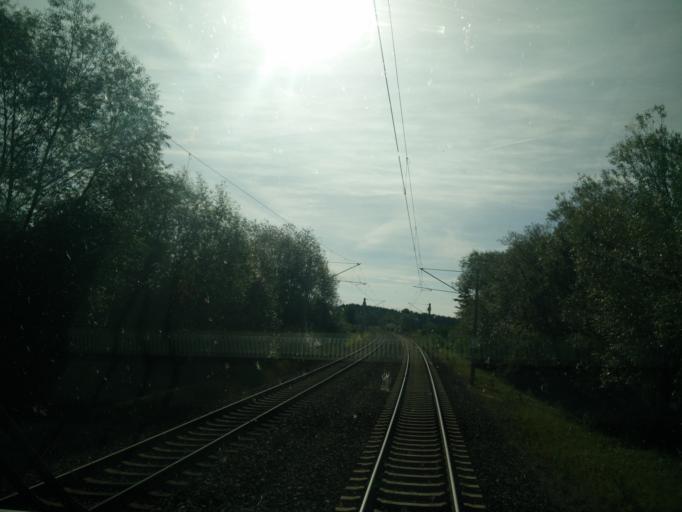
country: DE
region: Brandenburg
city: Luebben
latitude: 51.9583
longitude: 13.8278
